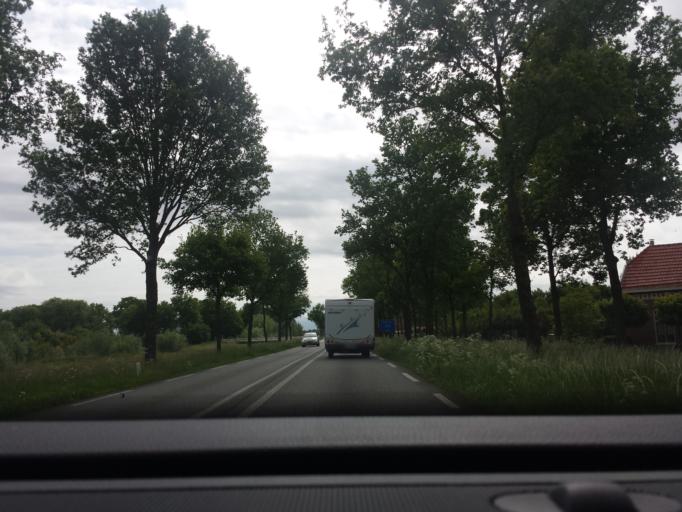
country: NL
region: Gelderland
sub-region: Oost Gelre
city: Lichtenvoorde
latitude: 52.0464
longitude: 6.5436
